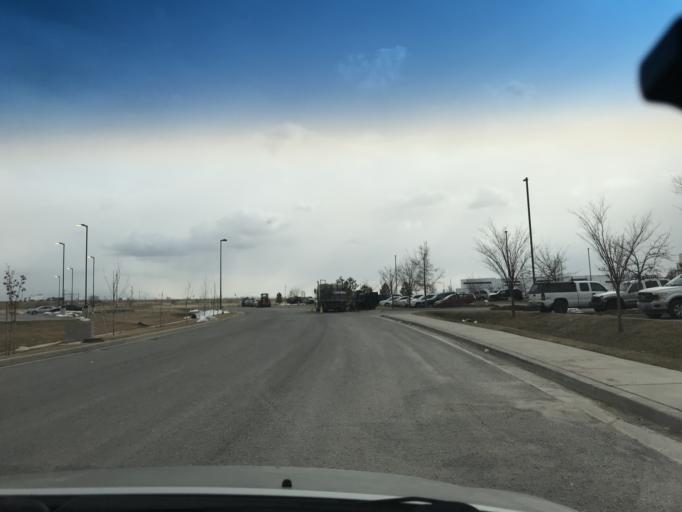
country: US
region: Utah
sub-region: Salt Lake County
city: West Valley City
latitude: 40.7739
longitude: -112.0304
